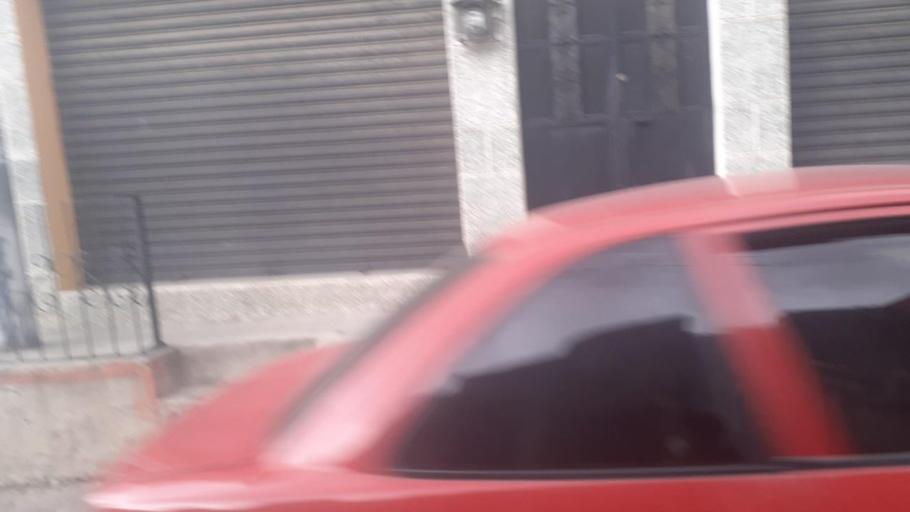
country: GT
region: Quetzaltenango
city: Quetzaltenango
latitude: 14.8369
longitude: -91.5202
